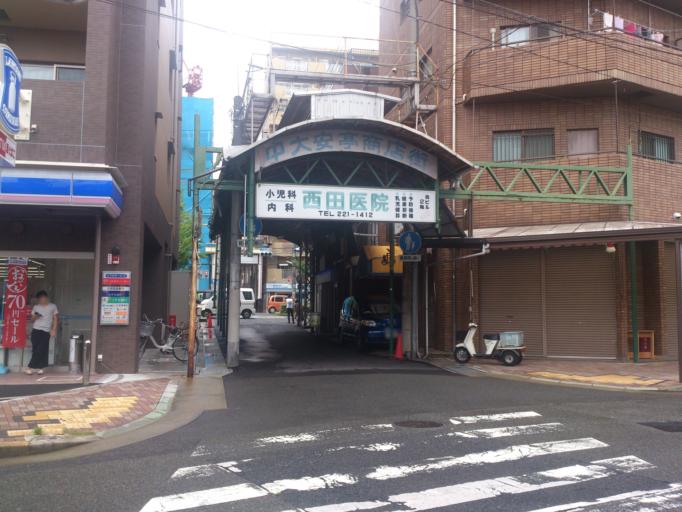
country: JP
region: Hyogo
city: Kobe
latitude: 34.7010
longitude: 135.2028
